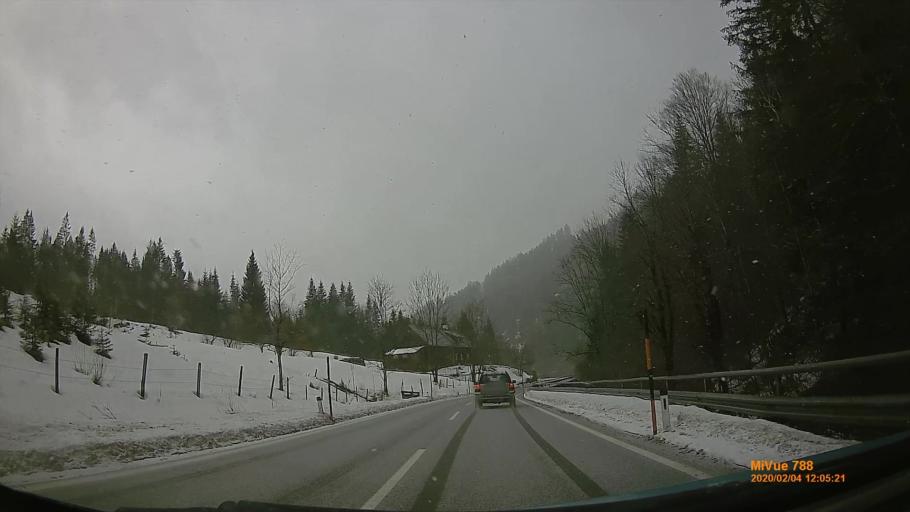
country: AT
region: Styria
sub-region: Politischer Bezirk Bruck-Muerzzuschlag
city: Muerzsteg
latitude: 47.7670
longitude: 15.4388
